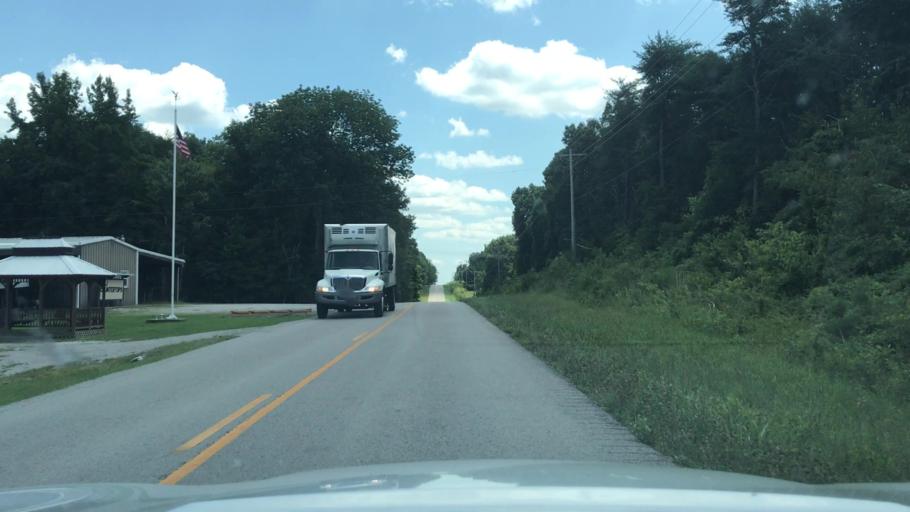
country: US
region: Kentucky
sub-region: Christian County
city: Hopkinsville
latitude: 36.9981
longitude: -87.3657
